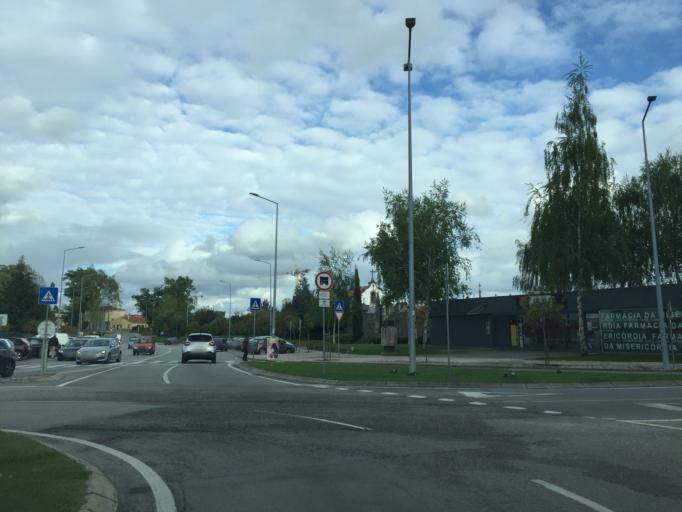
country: PT
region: Viseu
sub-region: Viseu
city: Viseu
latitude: 40.6531
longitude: -7.9131
